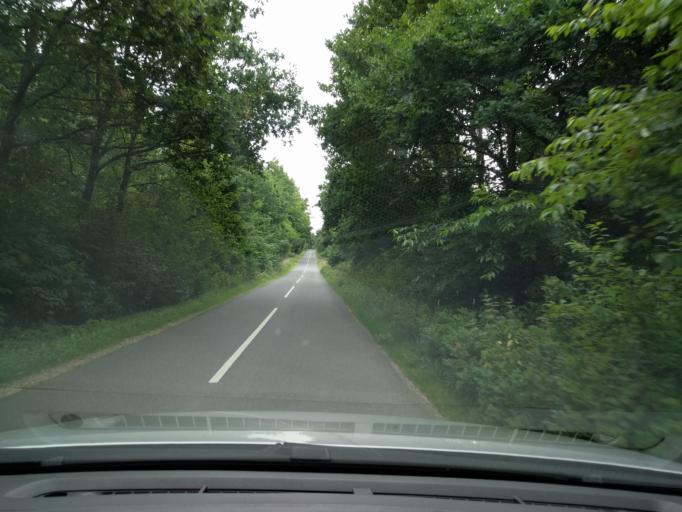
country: DK
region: Central Jutland
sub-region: Herning Kommune
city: Kibaek
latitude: 56.0384
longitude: 8.9047
